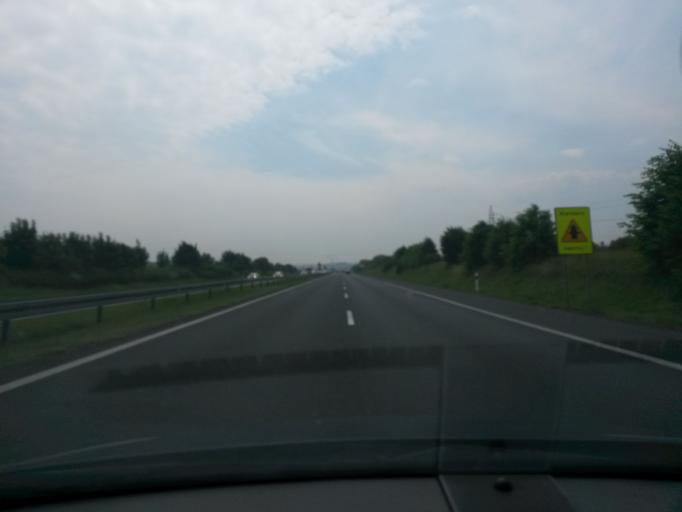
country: PL
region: Lodz Voivodeship
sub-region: Powiat piotrkowski
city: Wola Krzysztoporska
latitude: 51.3251
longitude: 19.5823
